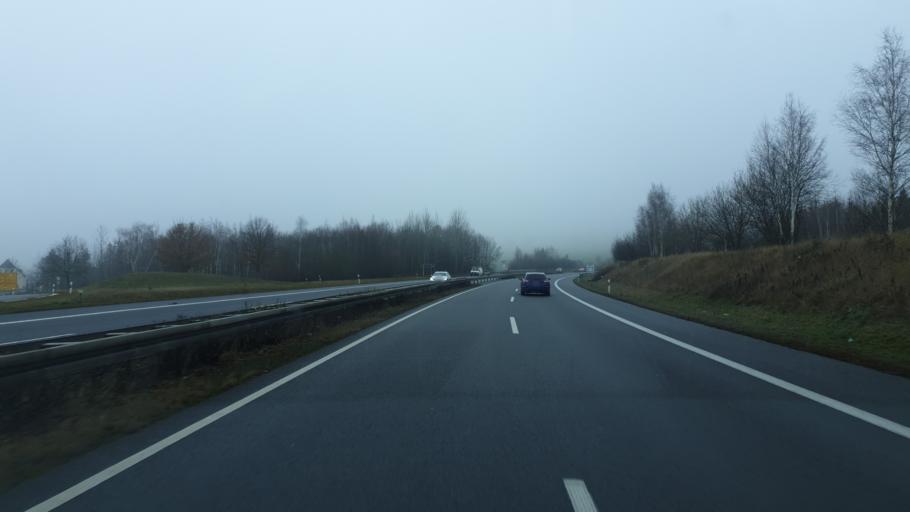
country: DE
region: Saxony
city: Gornau
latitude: 50.7577
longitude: 13.0166
